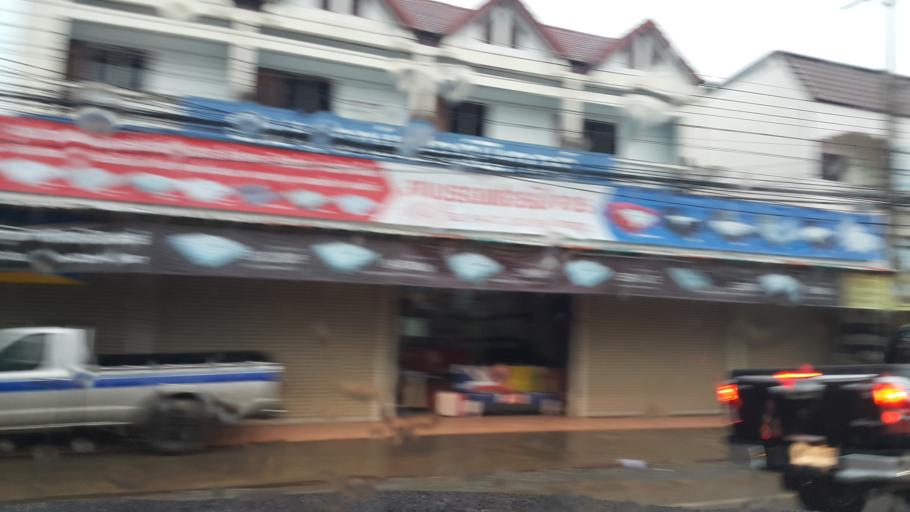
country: TH
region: Phayao
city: Chiang Kham
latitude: 19.5187
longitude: 100.3005
